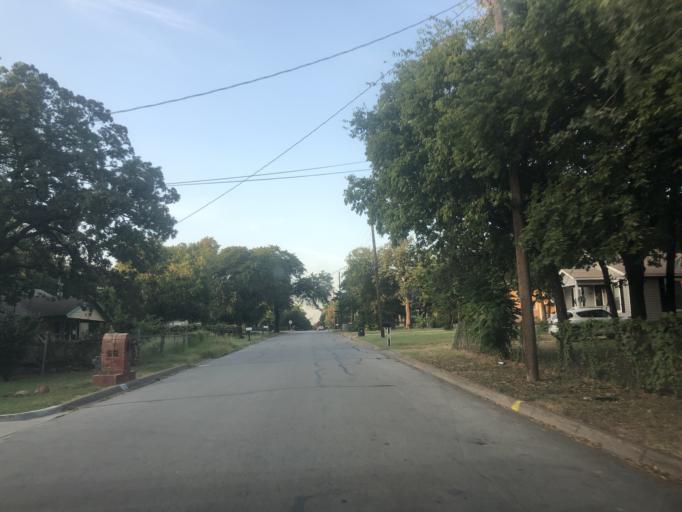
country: US
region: Texas
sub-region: Tarrant County
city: Lake Worth
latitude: 32.8034
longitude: -97.4496
